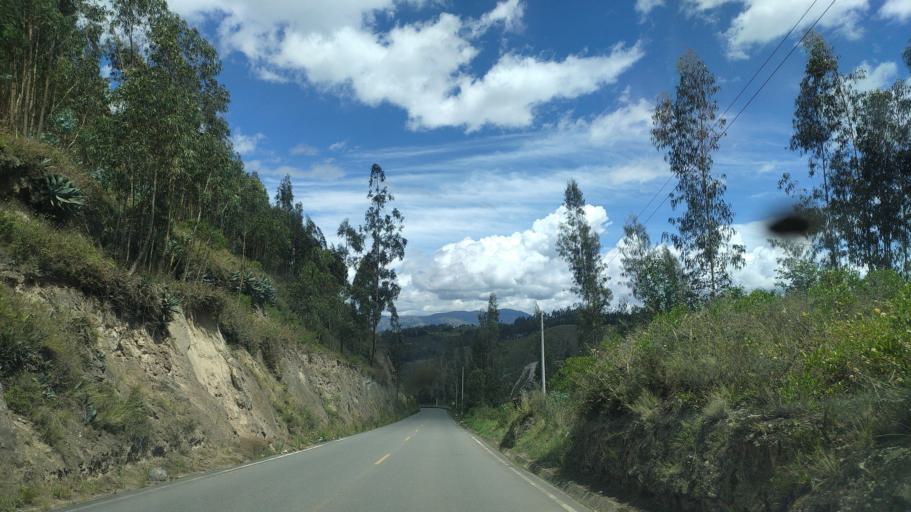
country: EC
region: Chimborazo
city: Riobamba
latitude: -1.6606
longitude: -78.5828
